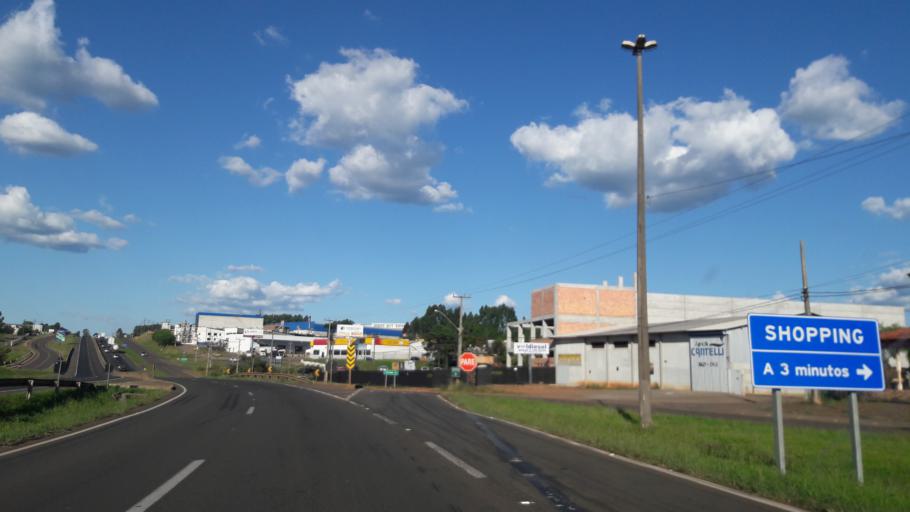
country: BR
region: Parana
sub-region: Guarapuava
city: Guarapuava
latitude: -25.3579
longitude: -51.4639
